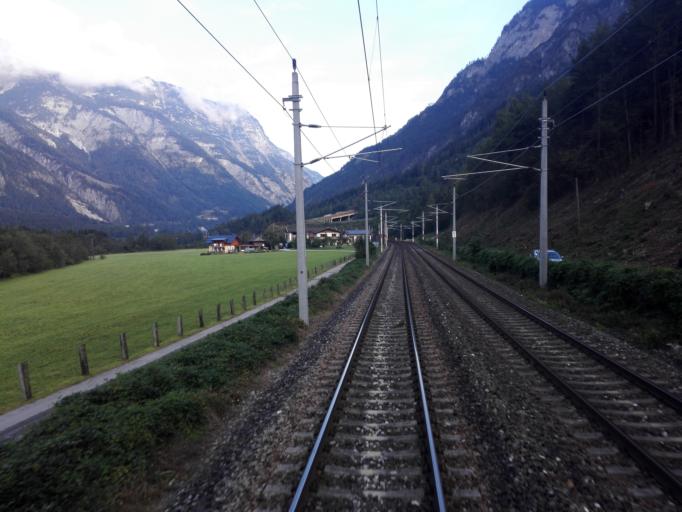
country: AT
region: Salzburg
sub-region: Politischer Bezirk Sankt Johann im Pongau
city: Werfen
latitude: 47.4988
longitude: 13.1776
